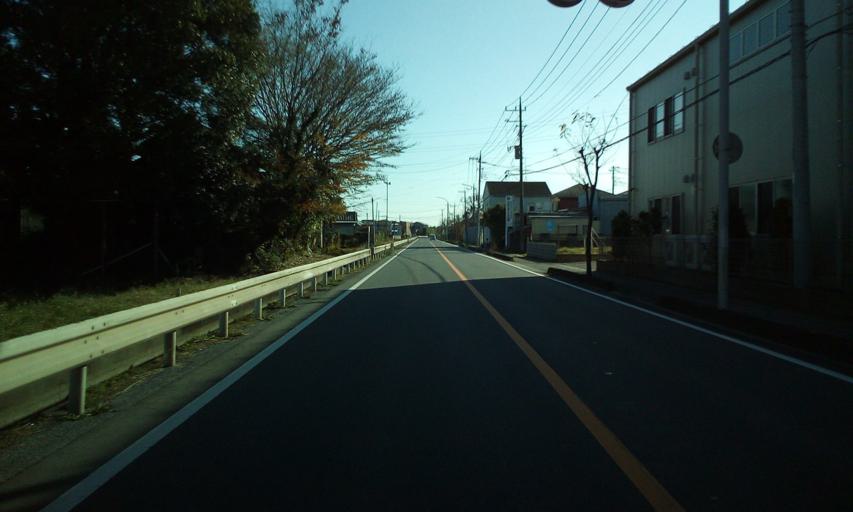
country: JP
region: Saitama
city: Kasukabe
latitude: 36.0061
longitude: 139.7947
